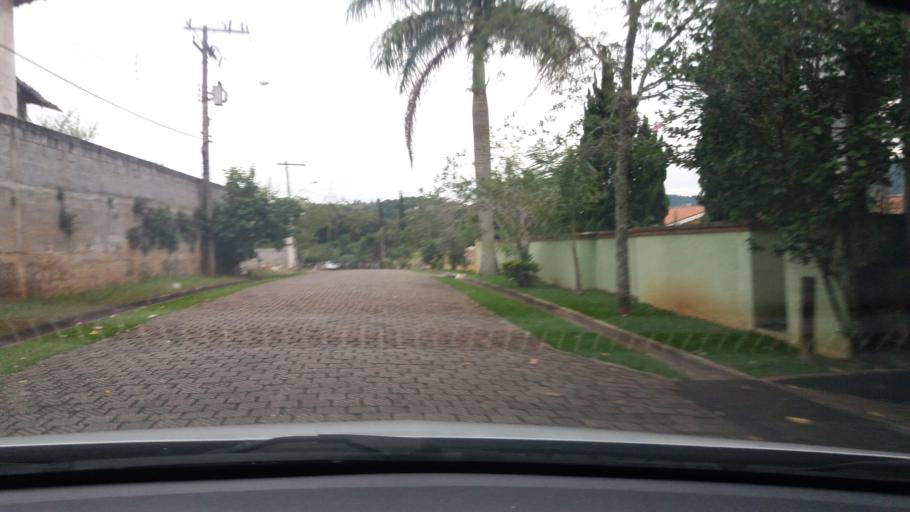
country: BR
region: Sao Paulo
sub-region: Bom Jesus Dos Perdoes
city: Bom Jesus dos Perdoes
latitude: -23.1713
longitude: -46.4537
